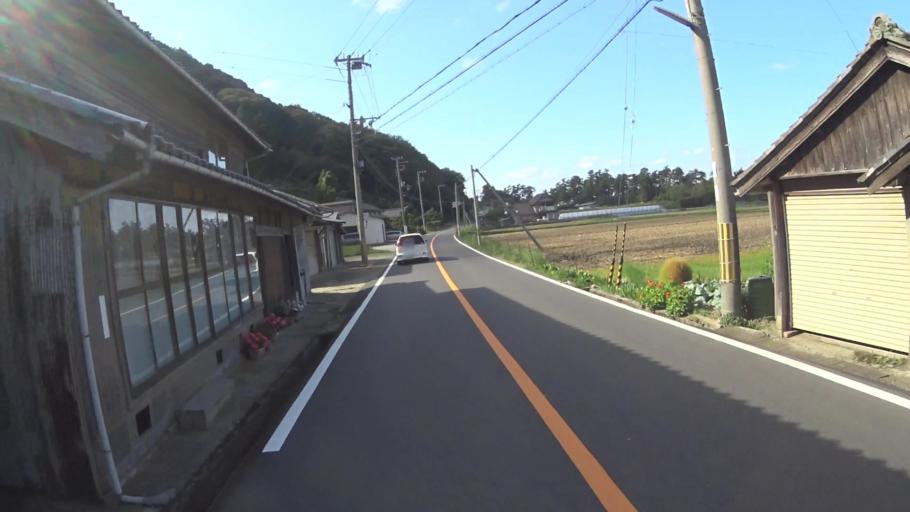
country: JP
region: Kyoto
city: Miyazu
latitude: 35.7482
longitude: 135.1619
